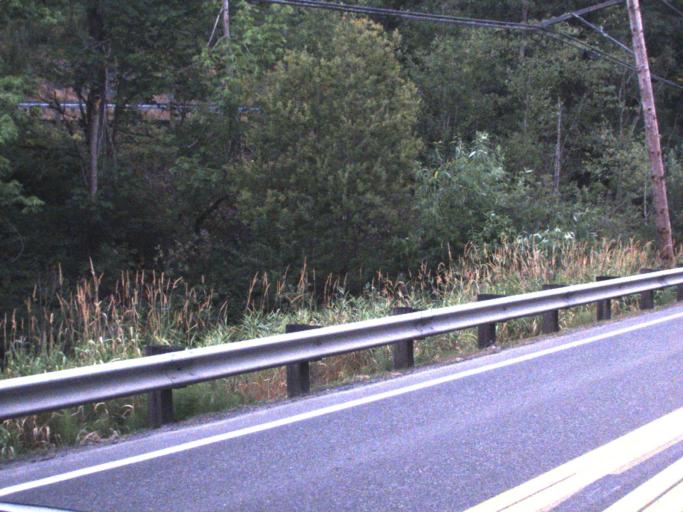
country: US
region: Washington
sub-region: King County
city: Lake Marcel-Stillwater
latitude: 47.6869
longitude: -121.9350
